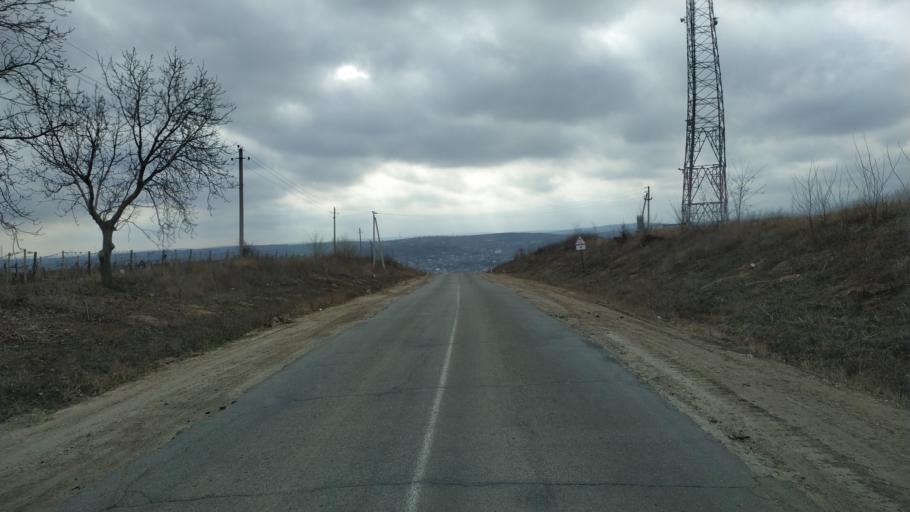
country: MD
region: Laloveni
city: Ialoveni
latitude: 46.8889
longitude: 28.7679
